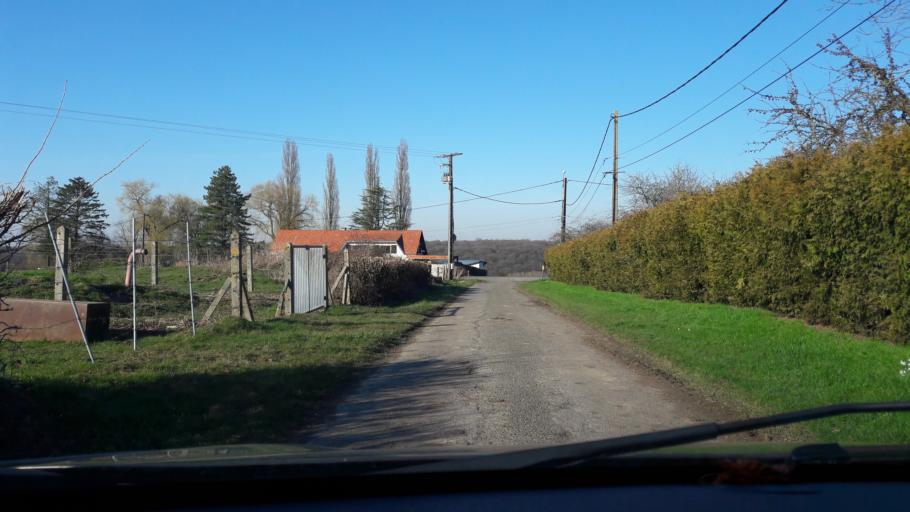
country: BE
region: Wallonia
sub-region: Province du Hainaut
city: Beaumont
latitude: 50.2512
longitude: 4.2062
